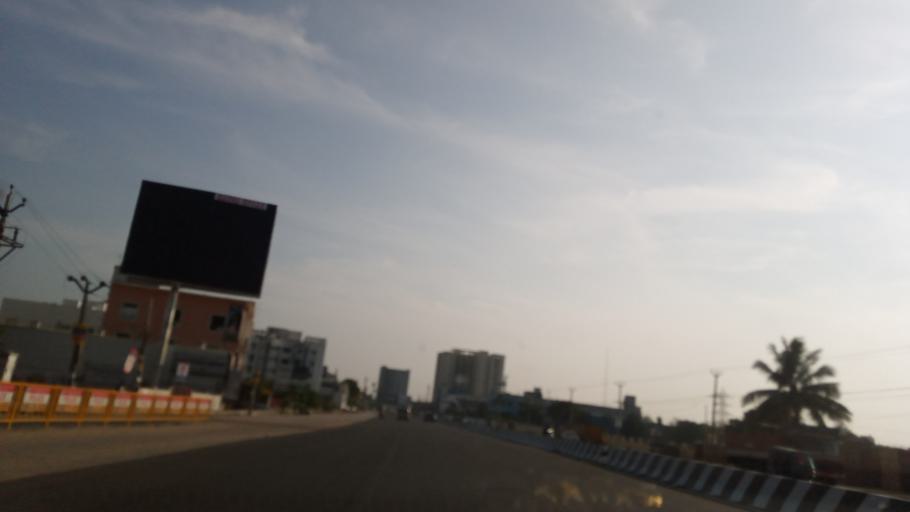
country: IN
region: Tamil Nadu
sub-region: Kancheepuram
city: Poonamalle
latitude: 13.0516
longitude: 80.1228
